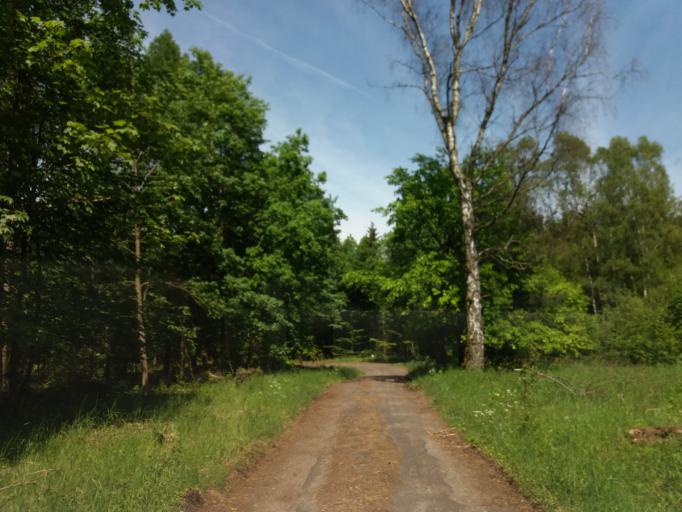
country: PL
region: West Pomeranian Voivodeship
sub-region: Powiat choszczenski
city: Recz
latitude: 53.3442
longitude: 15.5188
